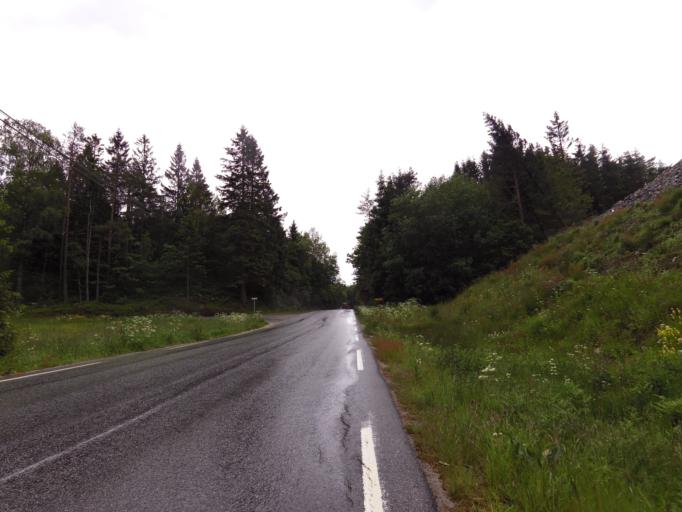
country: NO
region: Vest-Agder
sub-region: Mandal
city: Mandal
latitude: 58.0198
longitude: 7.5160
